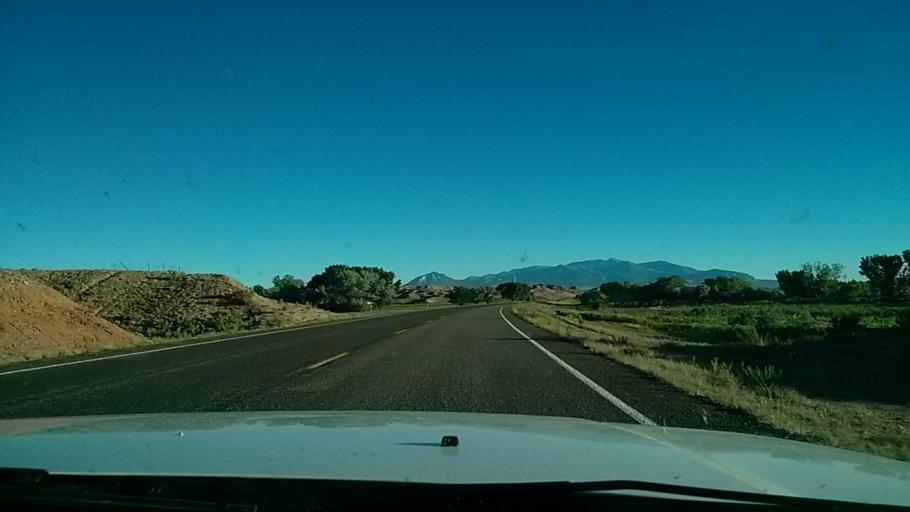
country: US
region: Utah
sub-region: Emery County
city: Ferron
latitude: 38.3957
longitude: -110.6932
